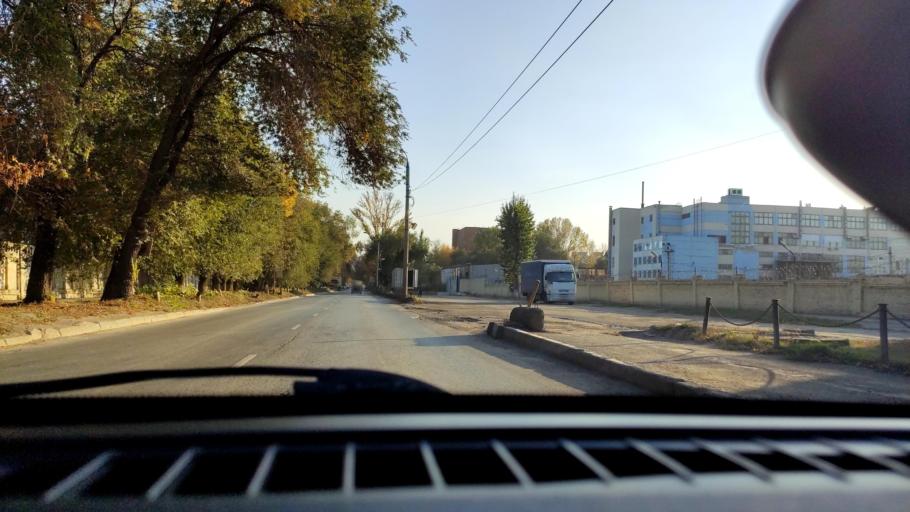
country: RU
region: Samara
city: Samara
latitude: 53.1924
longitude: 50.2453
